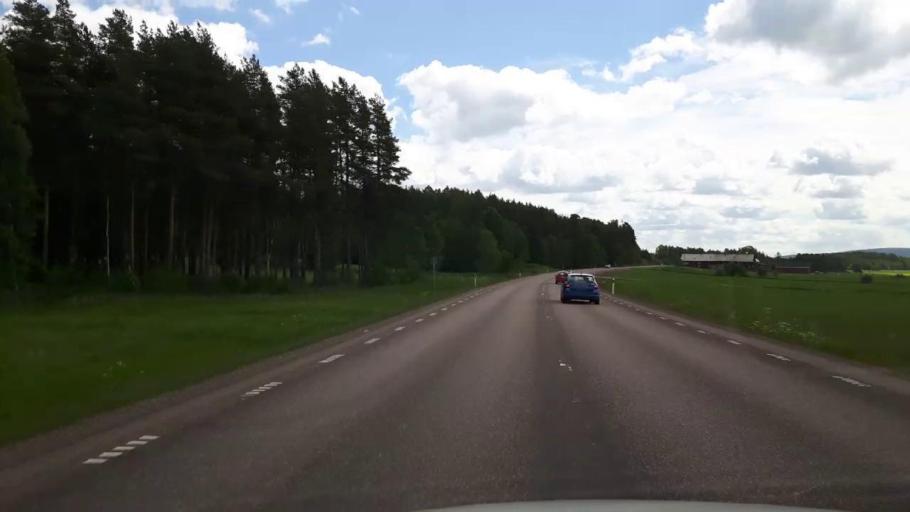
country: SE
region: Dalarna
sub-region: Saters Kommun
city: Saeter
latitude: 60.4399
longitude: 15.8174
